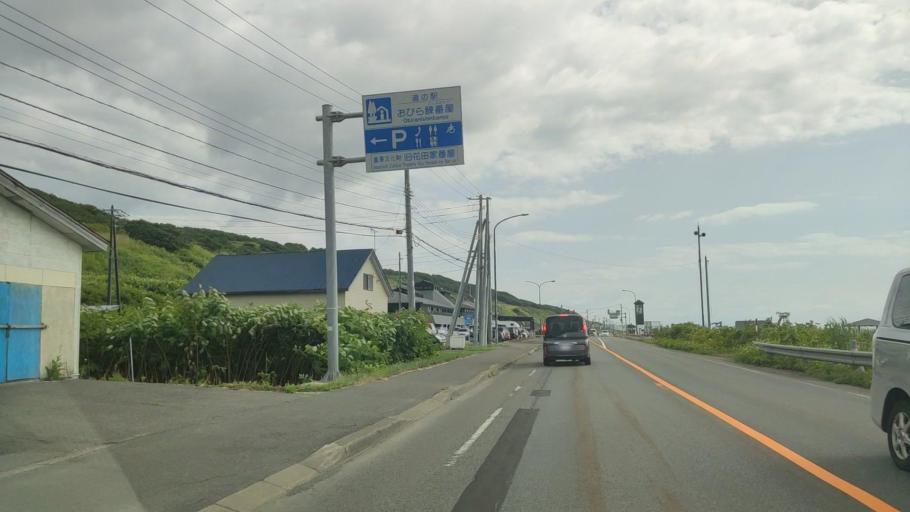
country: JP
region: Hokkaido
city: Rumoi
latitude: 44.1385
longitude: 141.6544
